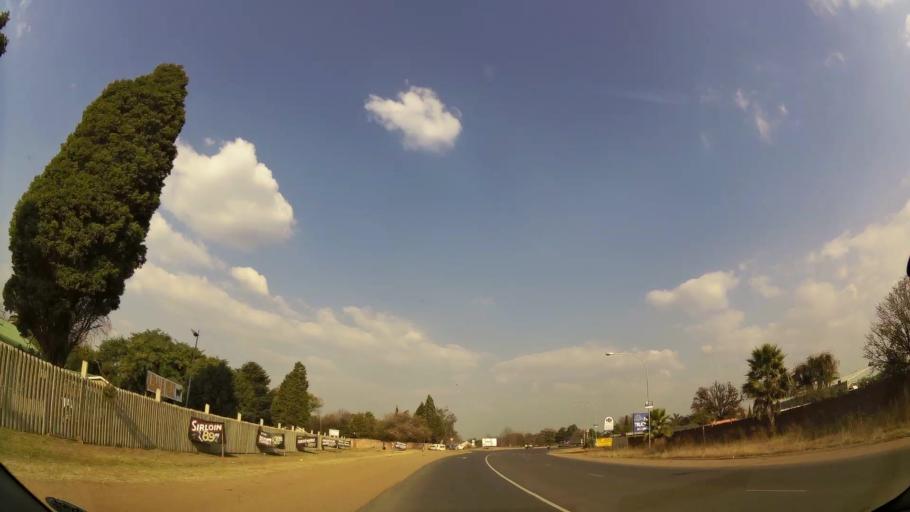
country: ZA
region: Gauteng
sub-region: Ekurhuleni Metropolitan Municipality
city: Benoni
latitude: -26.0945
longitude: 28.2969
